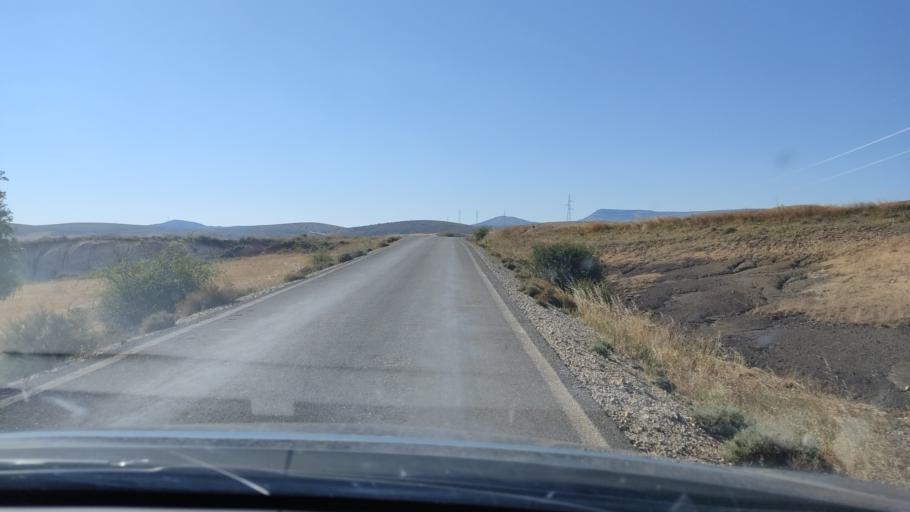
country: ES
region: Aragon
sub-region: Provincia de Teruel
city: Monforte de Moyuela
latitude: 41.0376
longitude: -0.9807
